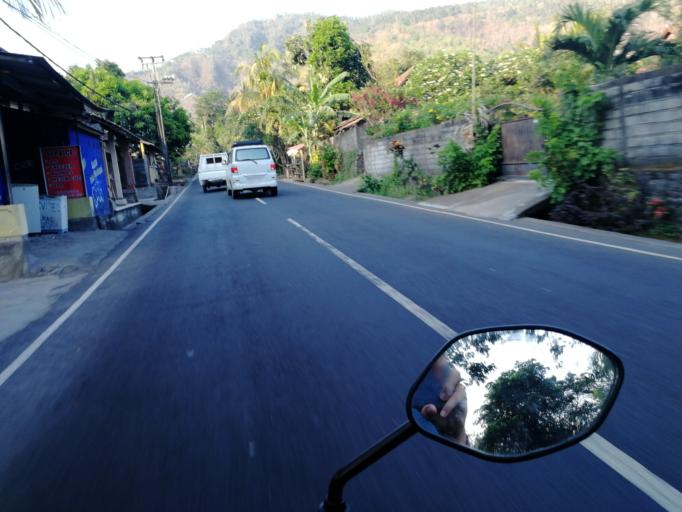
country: ID
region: Bali
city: Banjar Buayang
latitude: -8.3510
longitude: 115.6145
